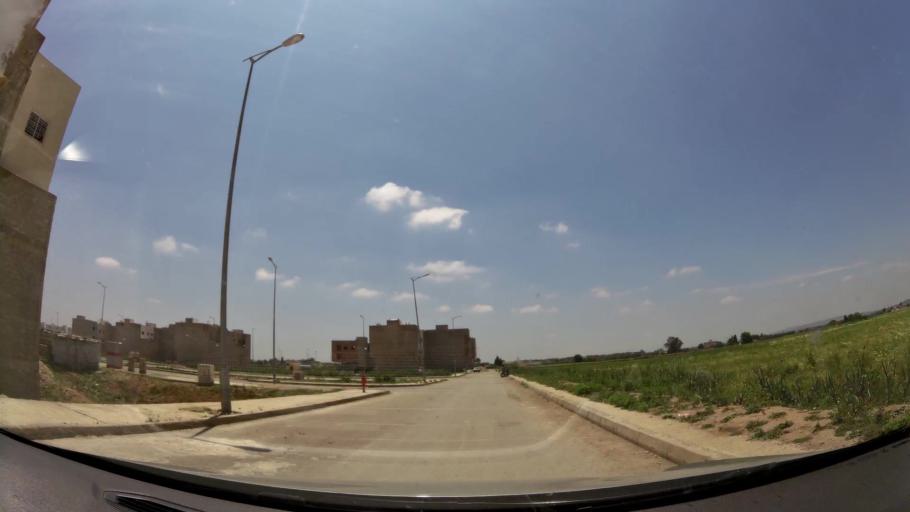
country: MA
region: Fes-Boulemane
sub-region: Fes
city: Fes
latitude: 34.0238
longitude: -5.0596
